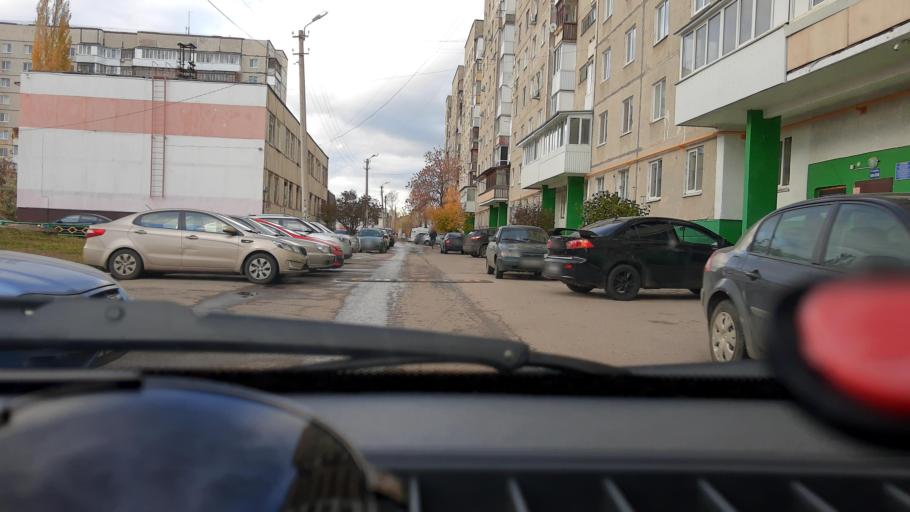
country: RU
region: Bashkortostan
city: Avdon
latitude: 54.7052
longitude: 55.8284
